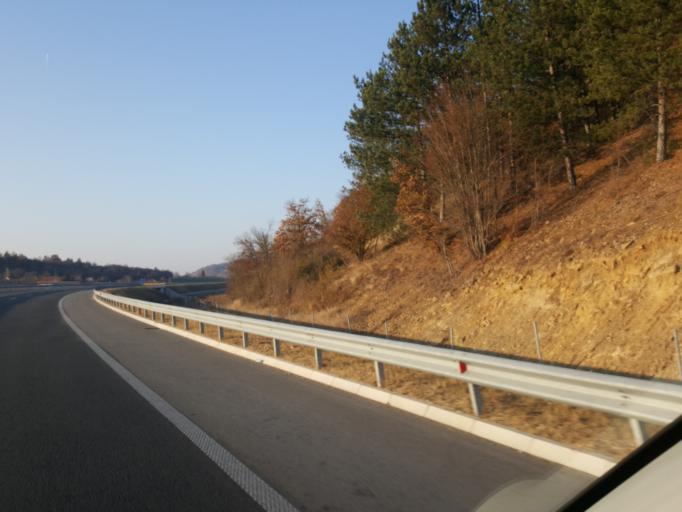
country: RS
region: Central Serbia
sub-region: Pirotski Okrug
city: Dimitrovgrad
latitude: 43.0248
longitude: 22.7261
